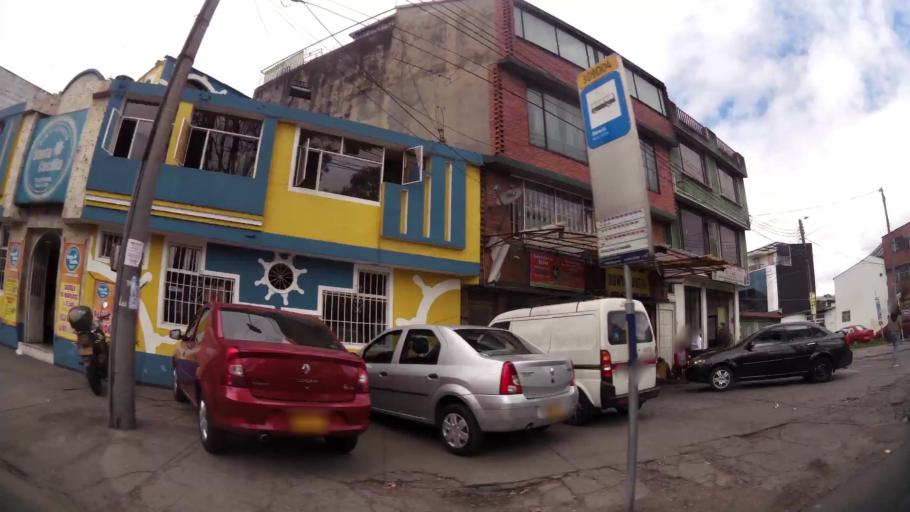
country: CO
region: Bogota D.C.
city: Barrio San Luis
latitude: 4.6947
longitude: -74.1042
